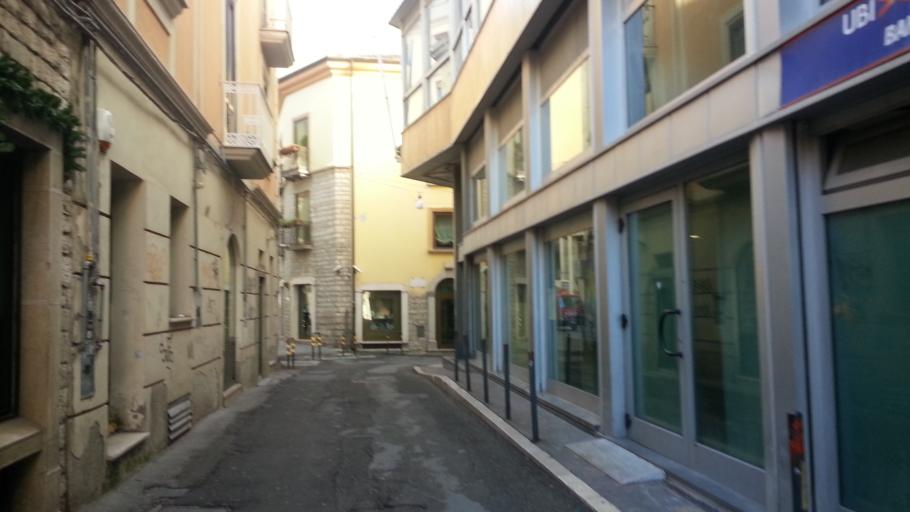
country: IT
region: Basilicate
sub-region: Provincia di Potenza
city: Potenza
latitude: 40.6386
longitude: 15.8031
